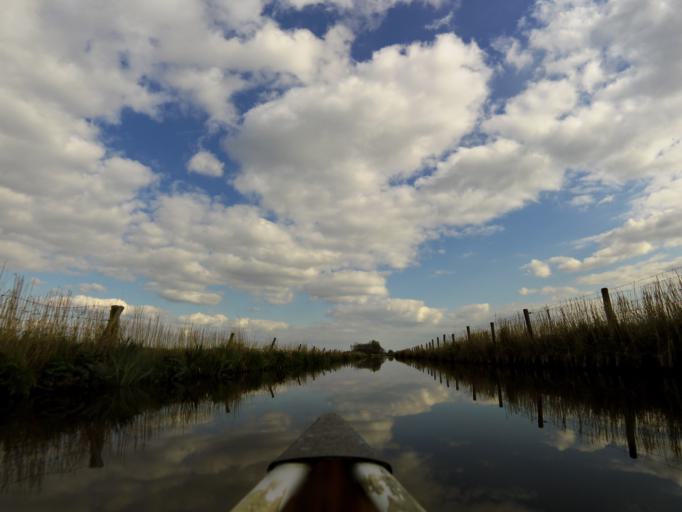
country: NL
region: South Holland
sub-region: Gemeente Leiderdorp
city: Leiderdorp
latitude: 52.1768
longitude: 4.5550
